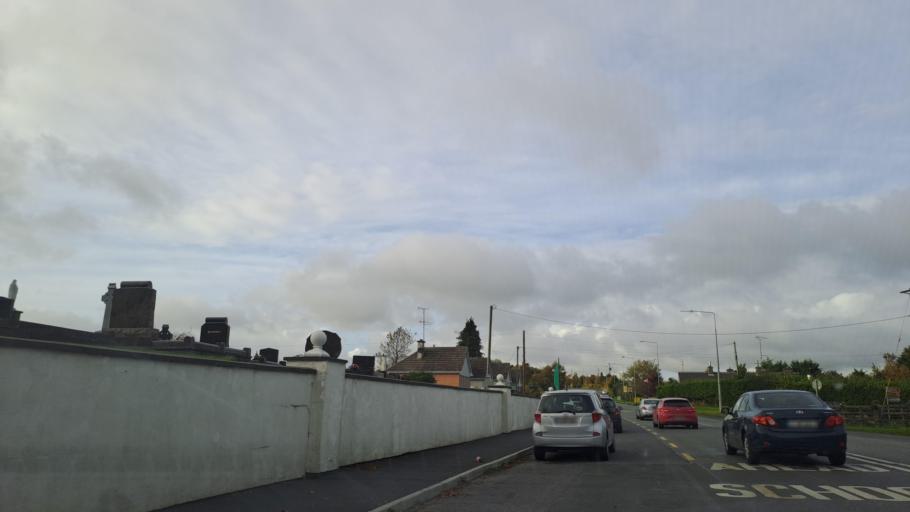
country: IE
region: Ulster
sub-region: An Cabhan
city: Kingscourt
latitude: 53.8153
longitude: -6.7398
